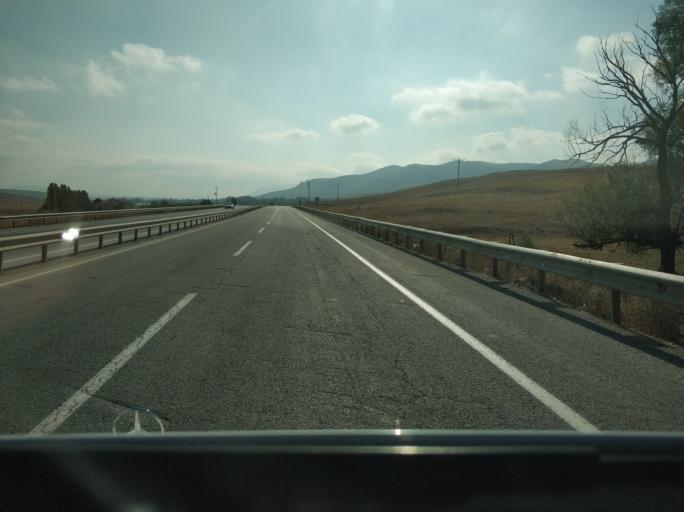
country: TR
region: Sivas
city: Yildizeli
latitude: 39.8359
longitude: 36.4416
